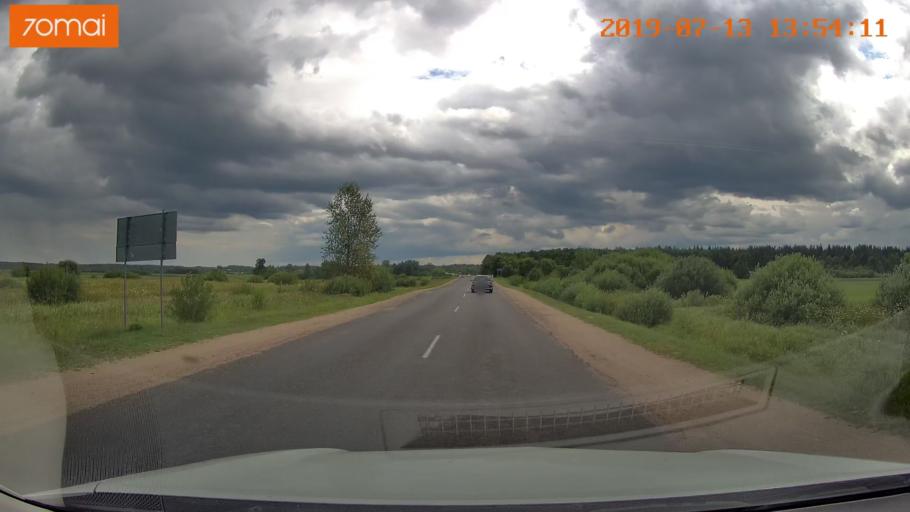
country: BY
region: Mogilev
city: Asipovichy
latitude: 53.2871
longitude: 28.6539
